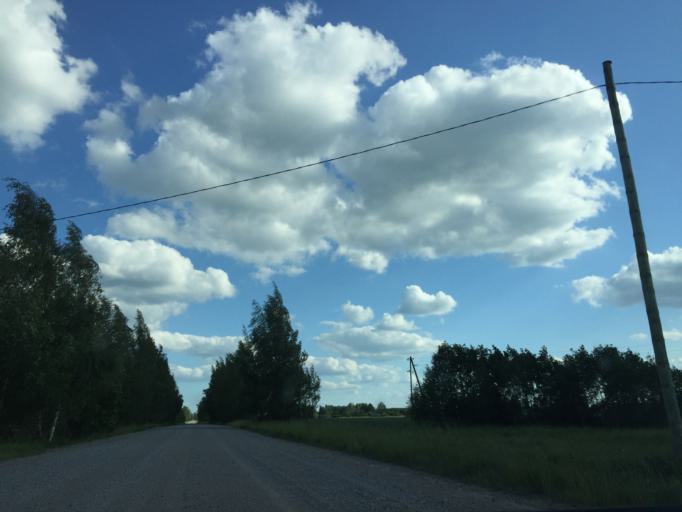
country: LV
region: Kandava
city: Kandava
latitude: 56.9212
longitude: 22.7895
